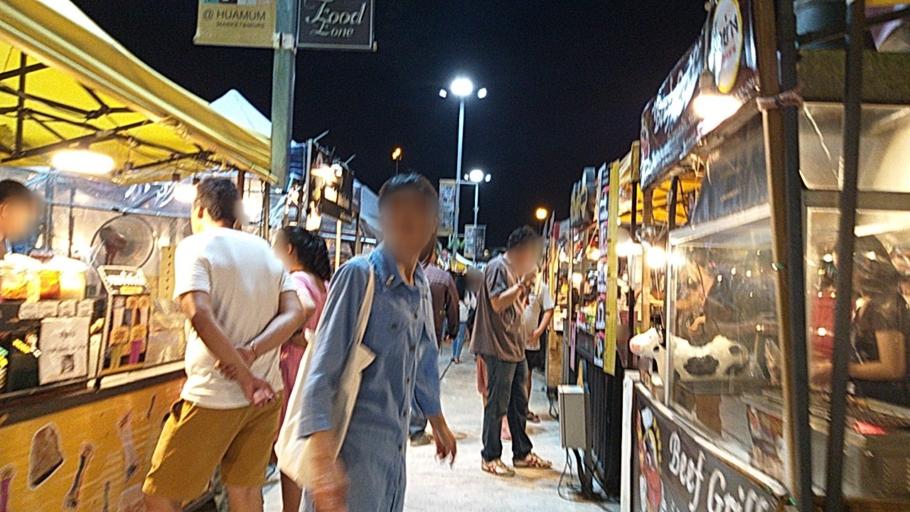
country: TH
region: Bangkok
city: Lat Phrao
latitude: 13.8266
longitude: 100.6264
